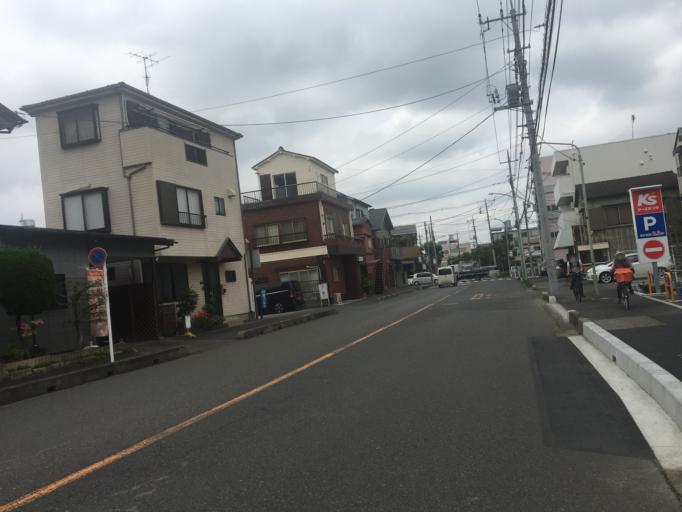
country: JP
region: Saitama
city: Kawaguchi
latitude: 35.8110
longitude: 139.7277
